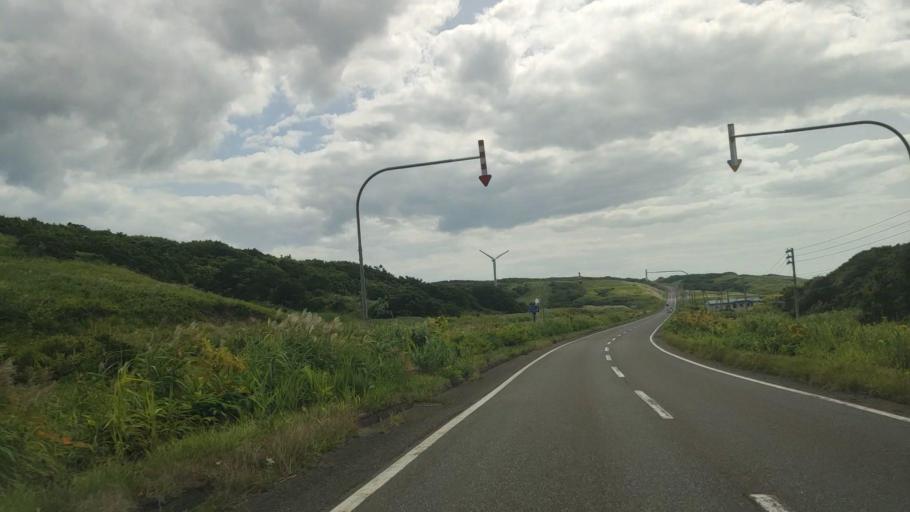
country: JP
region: Hokkaido
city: Rumoi
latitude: 44.5972
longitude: 141.7916
